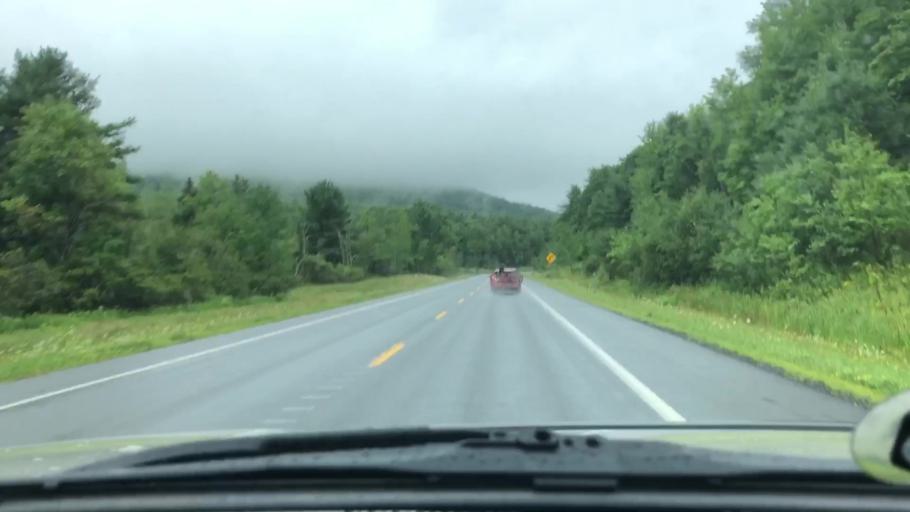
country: US
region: New York
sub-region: Greene County
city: Cairo
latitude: 42.3099
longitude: -74.1917
